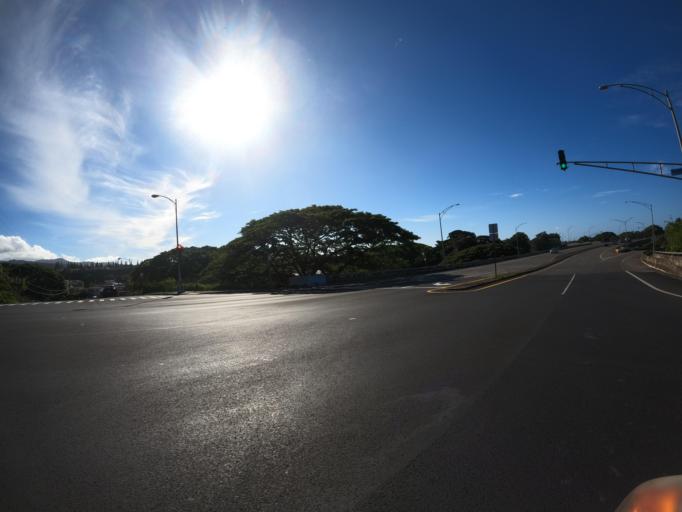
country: US
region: Hawaii
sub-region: Honolulu County
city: Halawa Heights
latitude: 21.3513
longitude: -157.8945
